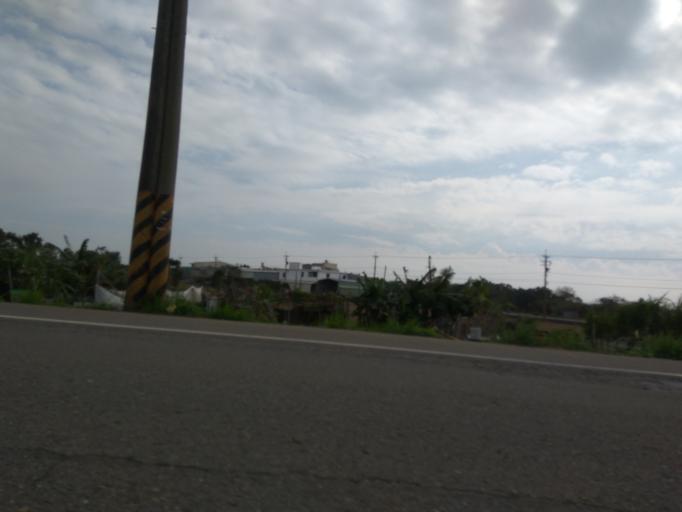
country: TW
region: Taiwan
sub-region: Hsinchu
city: Zhubei
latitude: 24.9499
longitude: 121.0095
